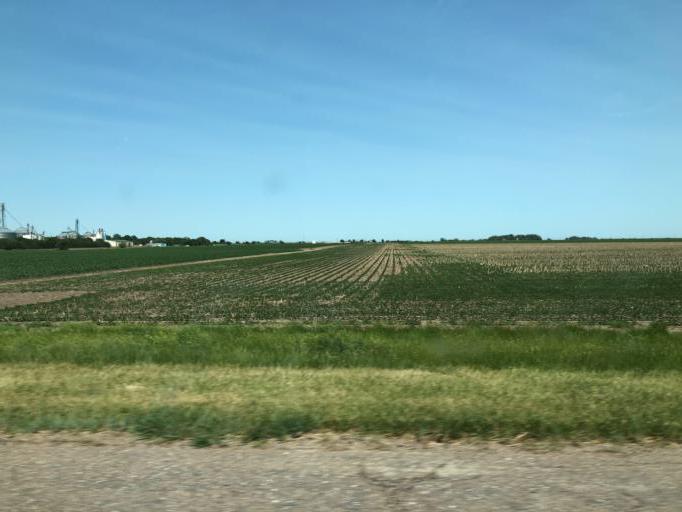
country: US
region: Nebraska
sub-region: Thayer County
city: Hebron
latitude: 40.3282
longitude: -97.5766
